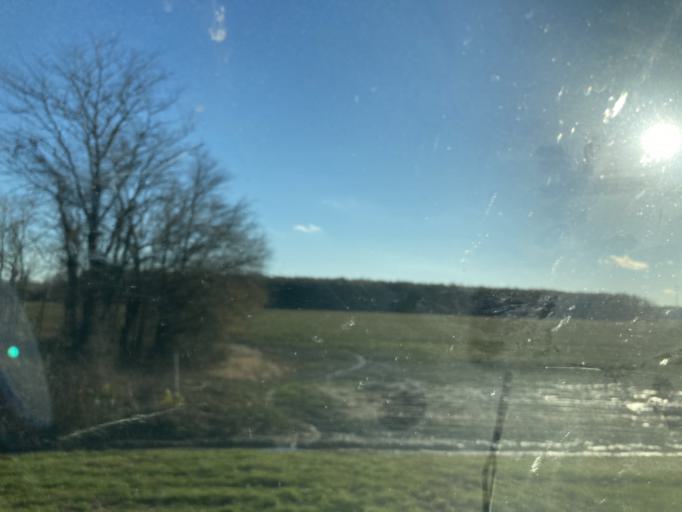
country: US
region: Mississippi
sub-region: Yazoo County
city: Yazoo City
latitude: 32.9256
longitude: -90.5761
